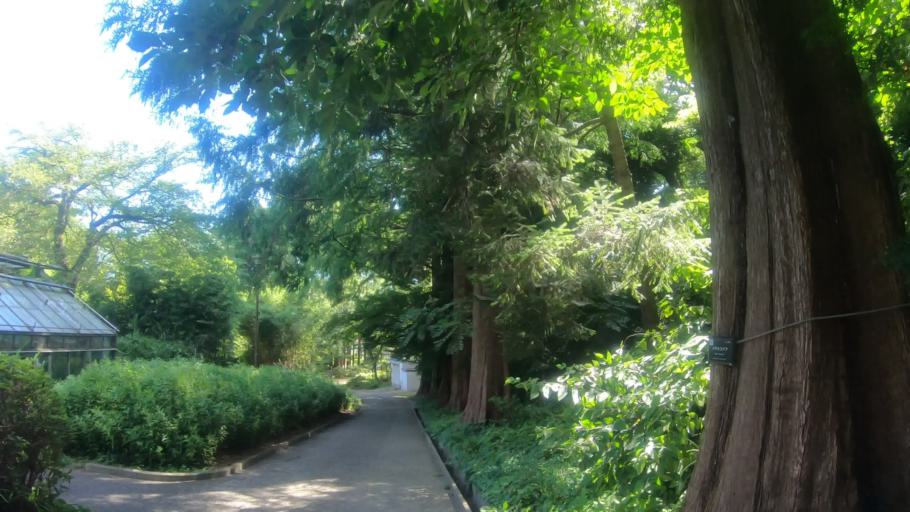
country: JP
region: Kanagawa
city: Yokohama
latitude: 35.4329
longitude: 139.5983
